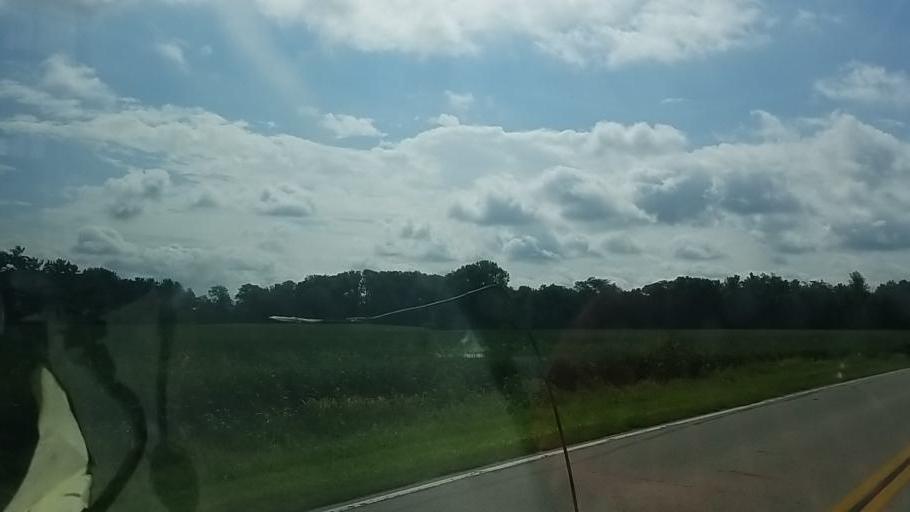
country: US
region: Ohio
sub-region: Pickaway County
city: Commercial Point
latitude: 39.7758
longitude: -83.1613
